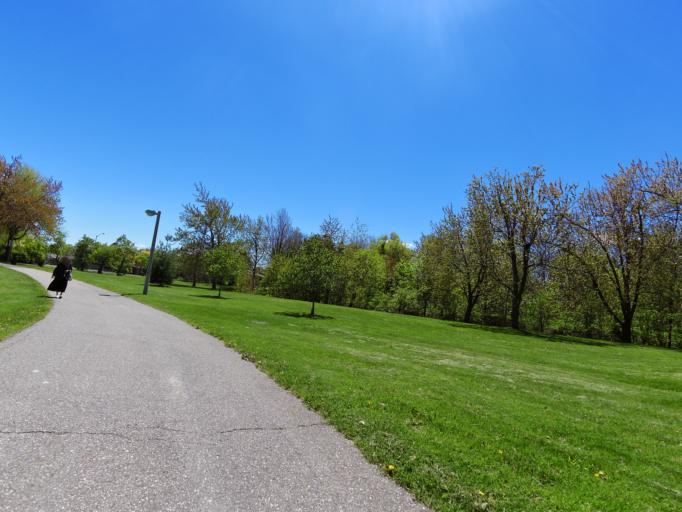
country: CA
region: Ontario
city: Brampton
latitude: 43.7134
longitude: -79.7090
